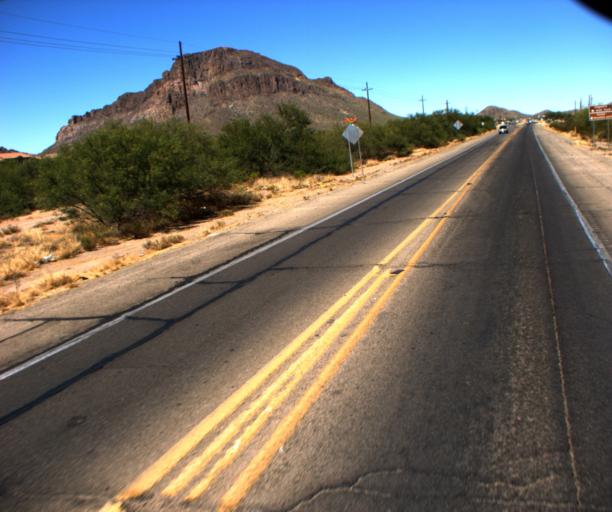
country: US
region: Arizona
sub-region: Pima County
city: Tucson Estates
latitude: 32.1700
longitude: -111.0762
